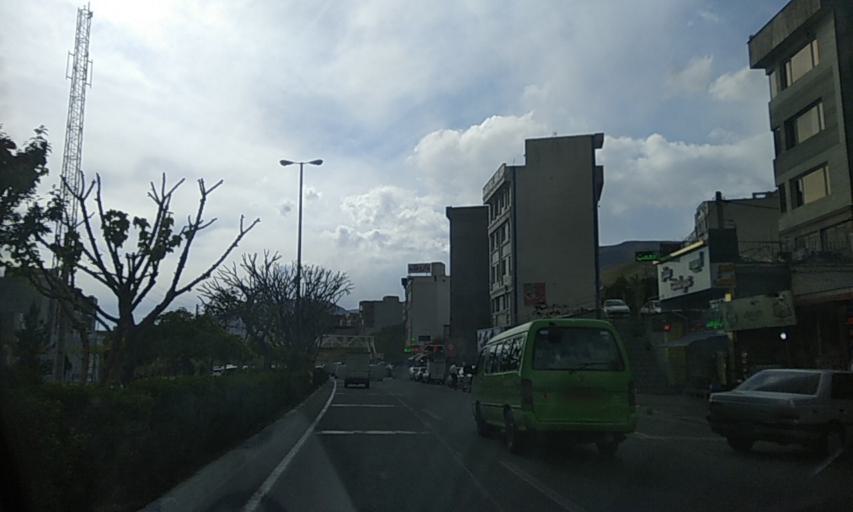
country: IR
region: Tehran
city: Tajrish
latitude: 35.7790
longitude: 51.3115
